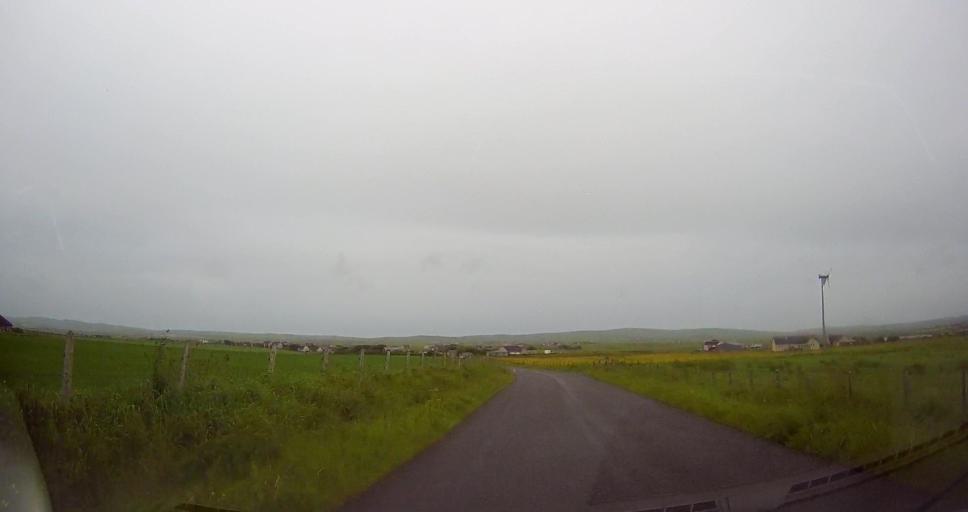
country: GB
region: Scotland
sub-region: Orkney Islands
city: Stromness
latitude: 59.0738
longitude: -3.2149
